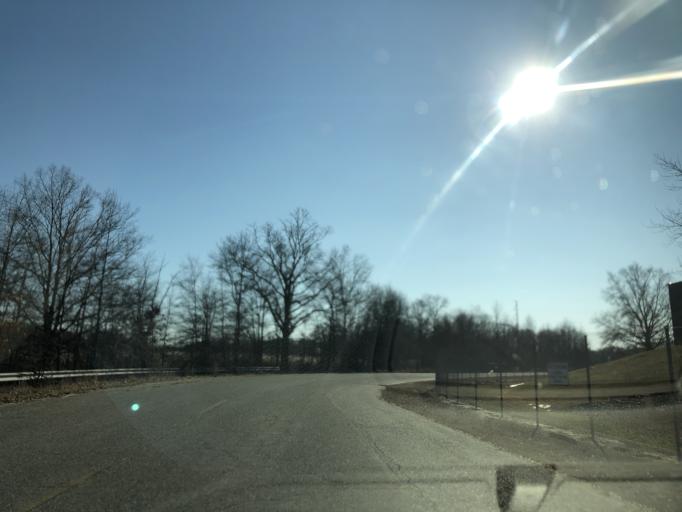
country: US
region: Pennsylvania
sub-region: Delaware County
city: Chester
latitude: 39.8107
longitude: -75.3508
